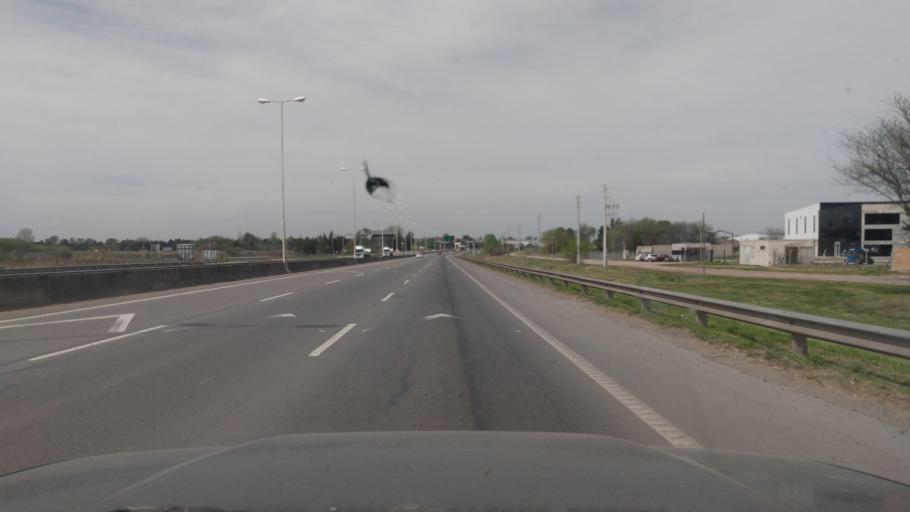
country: AR
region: Buenos Aires
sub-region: Partido de Pilar
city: Pilar
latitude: -34.4084
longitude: -59.0088
